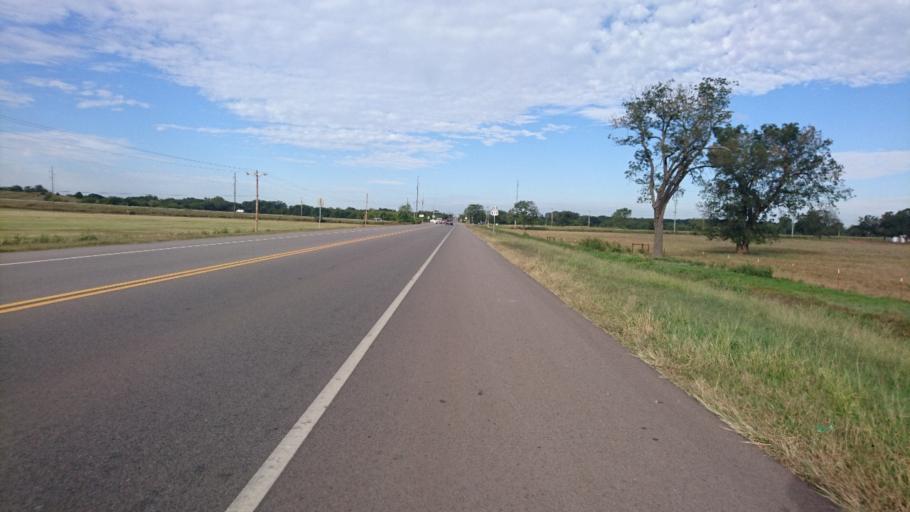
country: US
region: Oklahoma
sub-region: Lincoln County
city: Chandler
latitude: 35.6811
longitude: -97.0135
